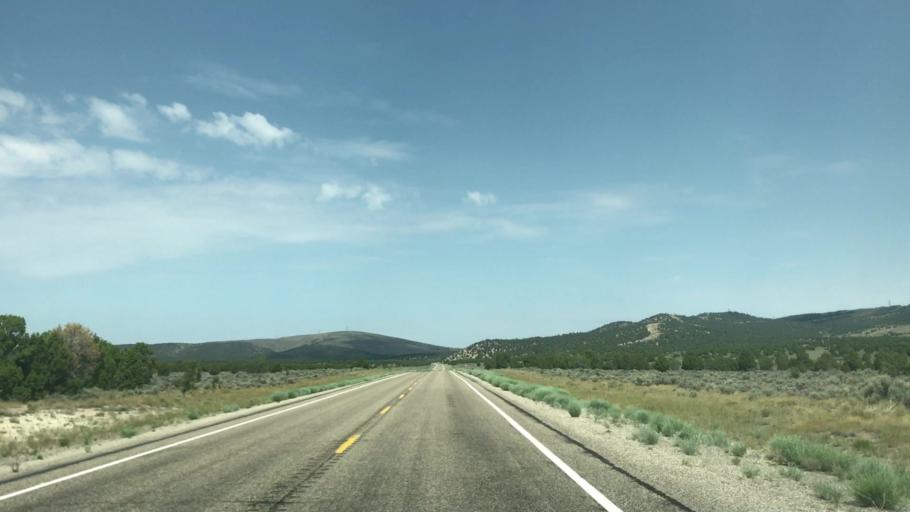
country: US
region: Nevada
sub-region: White Pine County
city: Ely
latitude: 39.3699
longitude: -115.0564
